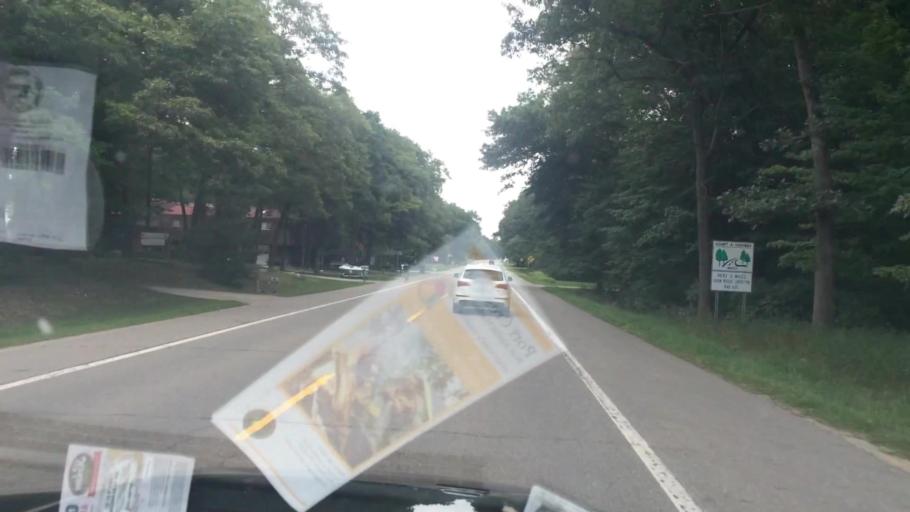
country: US
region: Michigan
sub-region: Huron County
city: Pigeon
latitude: 43.9811
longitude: -83.2044
